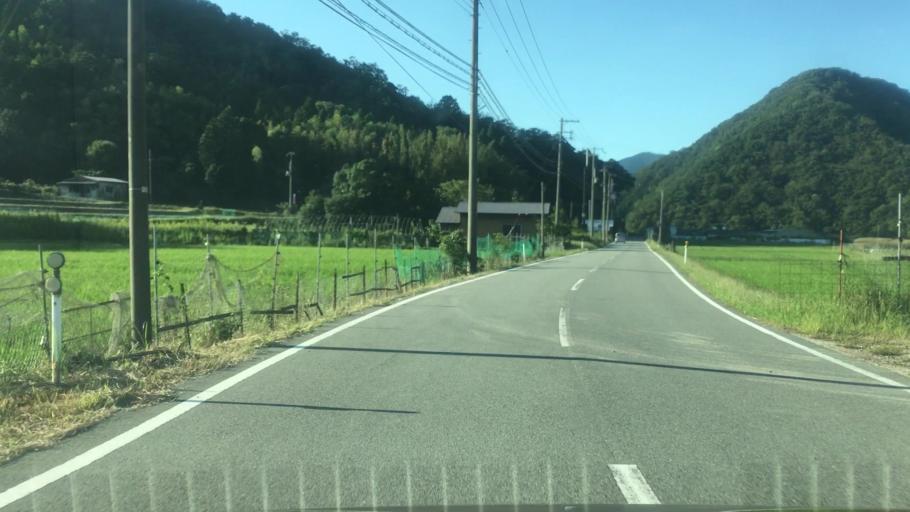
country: JP
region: Hyogo
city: Toyooka
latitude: 35.6124
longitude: 134.8282
